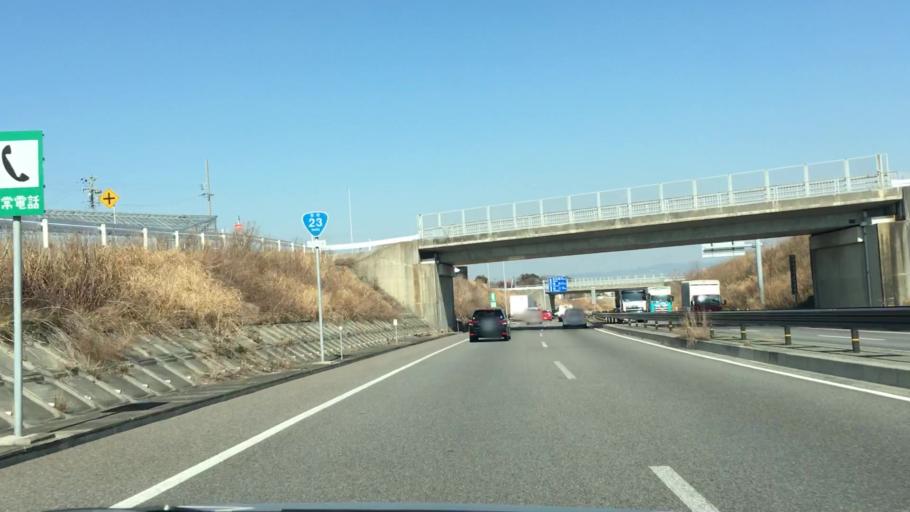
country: JP
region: Aichi
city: Toyohashi
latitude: 34.7121
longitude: 137.3520
